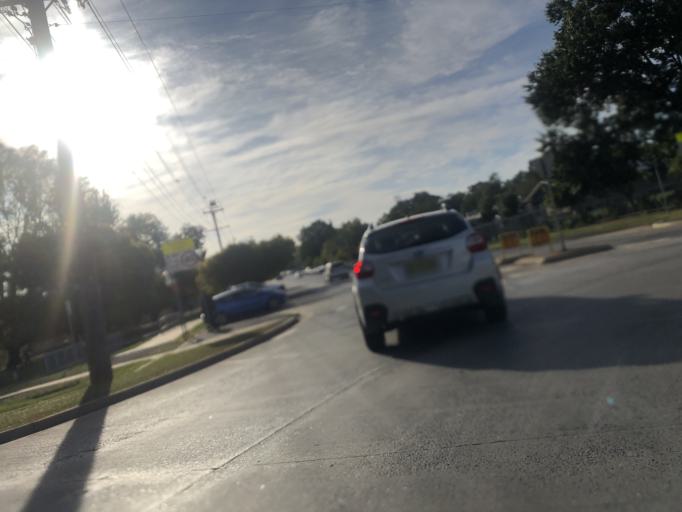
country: AU
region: New South Wales
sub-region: Orange Municipality
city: Orange
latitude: -33.2875
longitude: 149.0979
